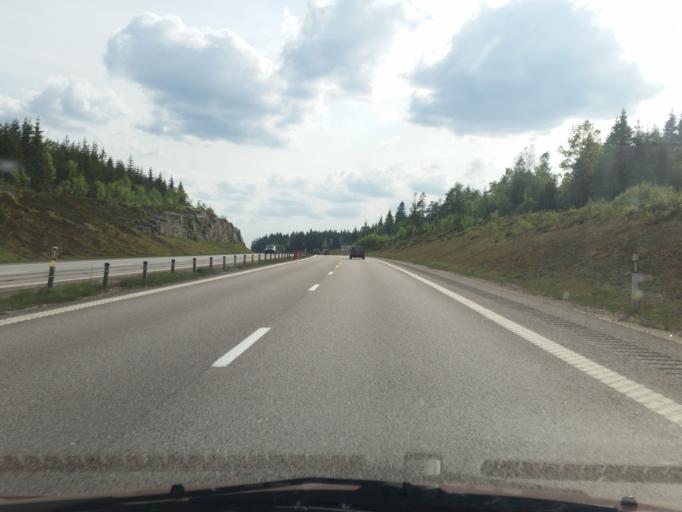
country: SE
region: Vaestra Goetaland
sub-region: Boras Kommun
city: Dalsjofors
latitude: 57.7521
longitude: 13.0768
